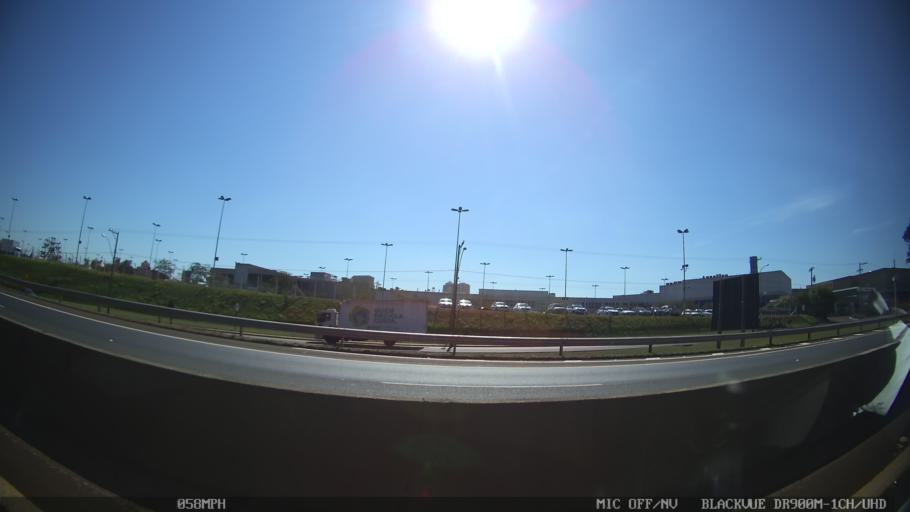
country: BR
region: Sao Paulo
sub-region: Ribeirao Preto
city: Ribeirao Preto
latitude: -21.2093
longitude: -47.7669
